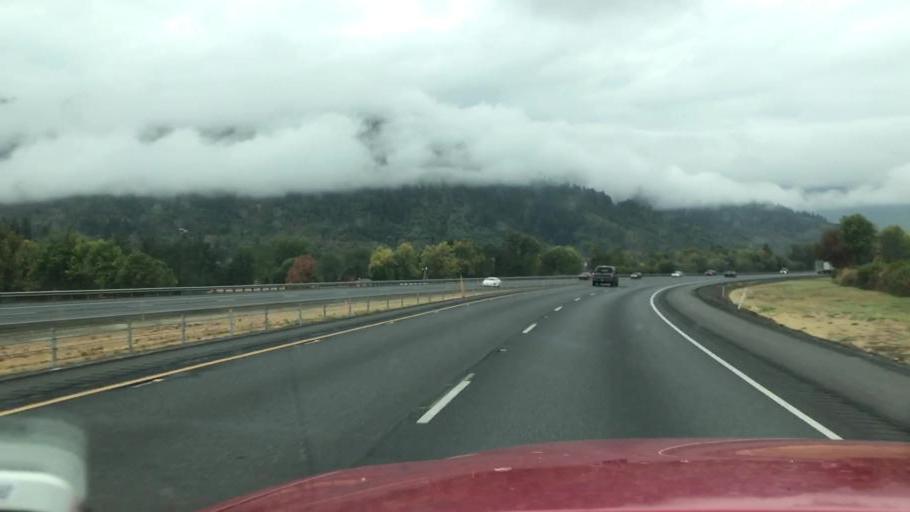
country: US
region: Oregon
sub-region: Jackson County
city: Rogue River
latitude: 42.4134
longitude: -123.1532
